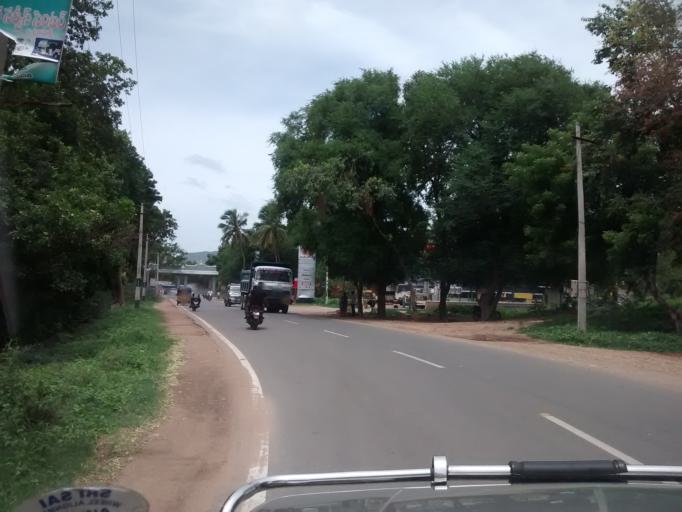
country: IN
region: Andhra Pradesh
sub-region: Chittoor
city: Narasingapuram
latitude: 13.6165
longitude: 79.3632
